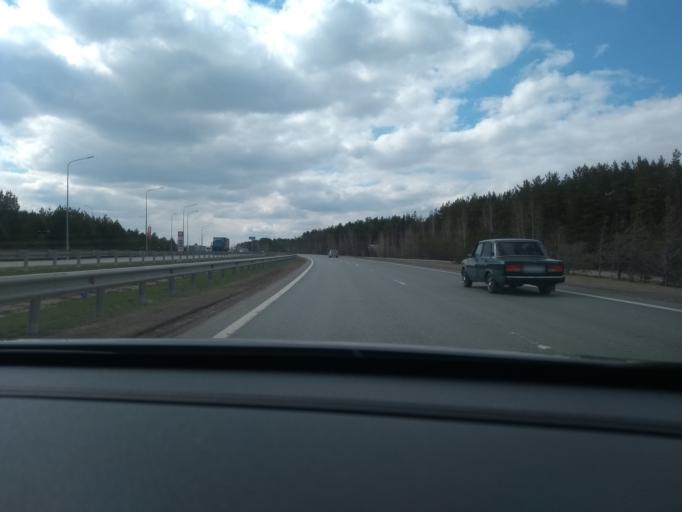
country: RU
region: Tatarstan
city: Yelabuga
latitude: 55.7810
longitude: 52.1936
